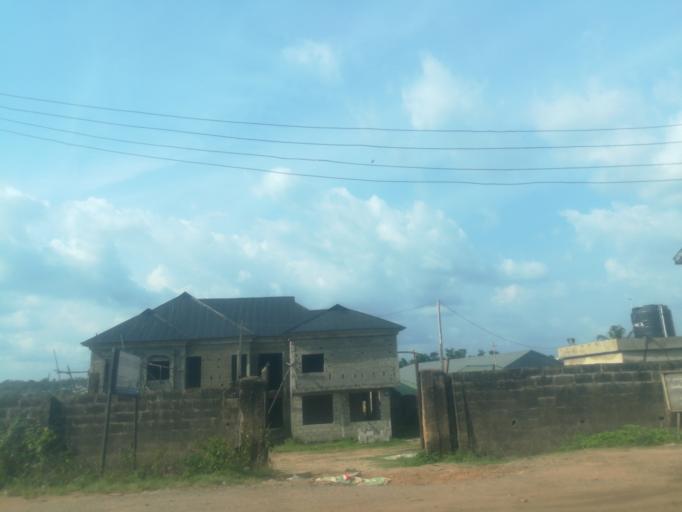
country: NG
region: Oyo
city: Ido
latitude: 7.3959
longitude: 3.7844
